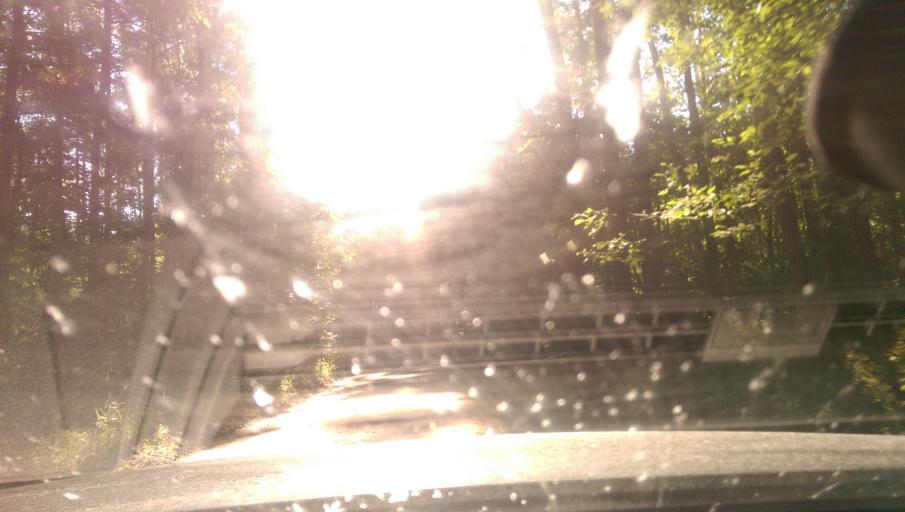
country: LT
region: Klaipedos apskritis
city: Gargzdai
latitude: 55.6635
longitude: 21.3579
